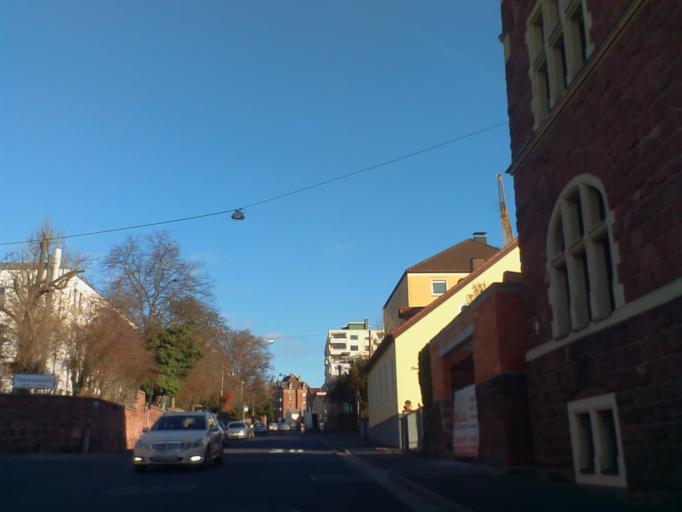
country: DE
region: Bavaria
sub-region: Regierungsbezirk Unterfranken
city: Bad Kissingen
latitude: 50.2029
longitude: 10.0785
